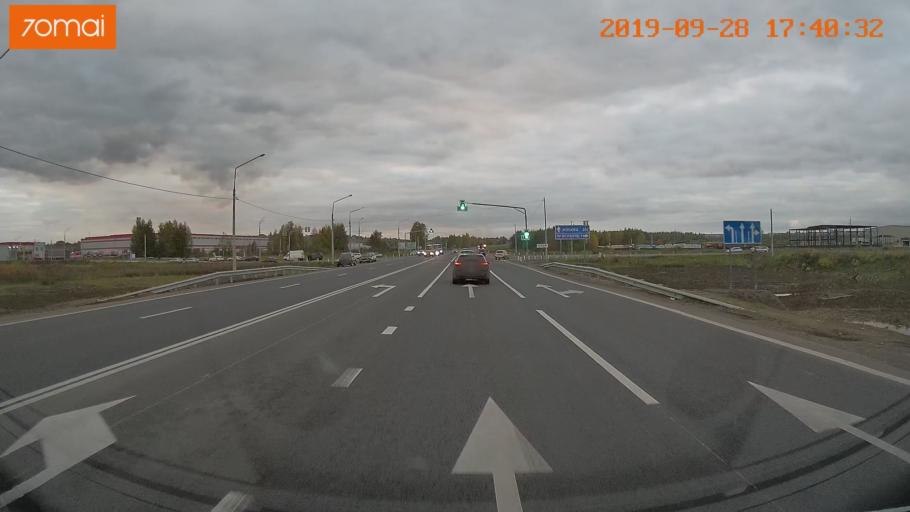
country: RU
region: Jaroslavl
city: Yaroslavl
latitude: 57.5504
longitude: 39.8925
